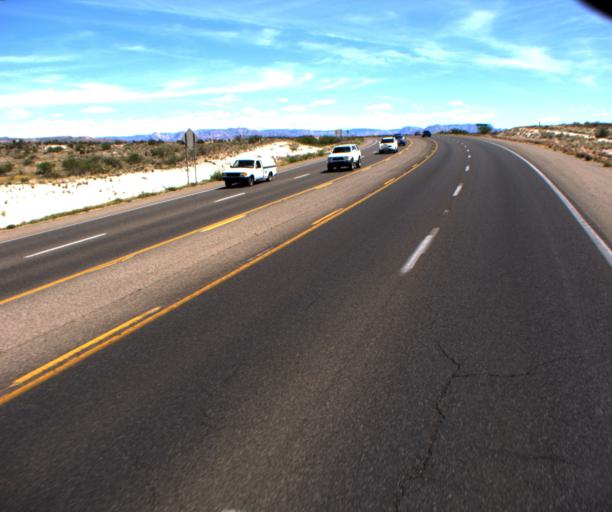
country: US
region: Arizona
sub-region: Yavapai County
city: Verde Village
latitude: 34.7228
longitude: -111.9857
